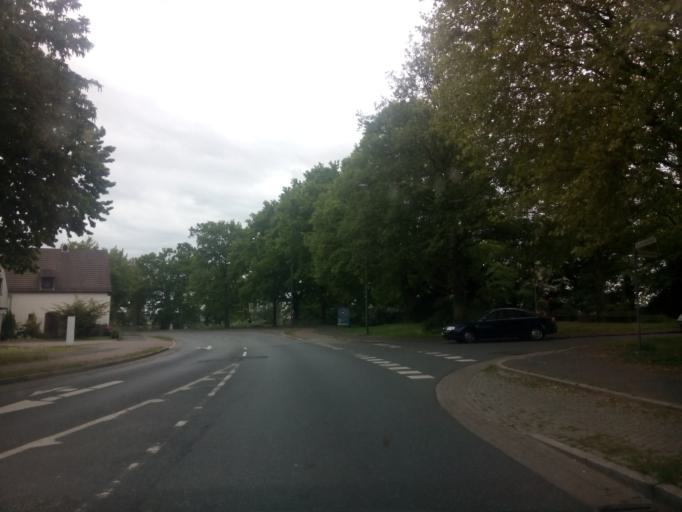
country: DE
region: Lower Saxony
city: Neuenkirchen
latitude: 53.1855
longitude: 8.5557
